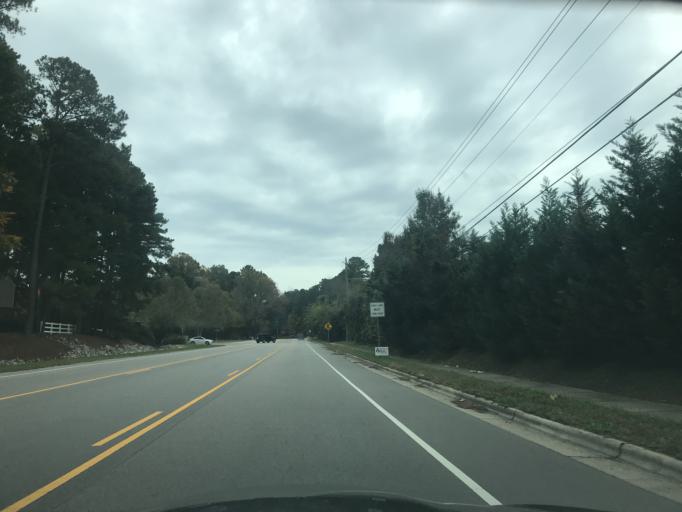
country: US
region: North Carolina
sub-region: Wake County
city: West Raleigh
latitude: 35.8798
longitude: -78.5978
